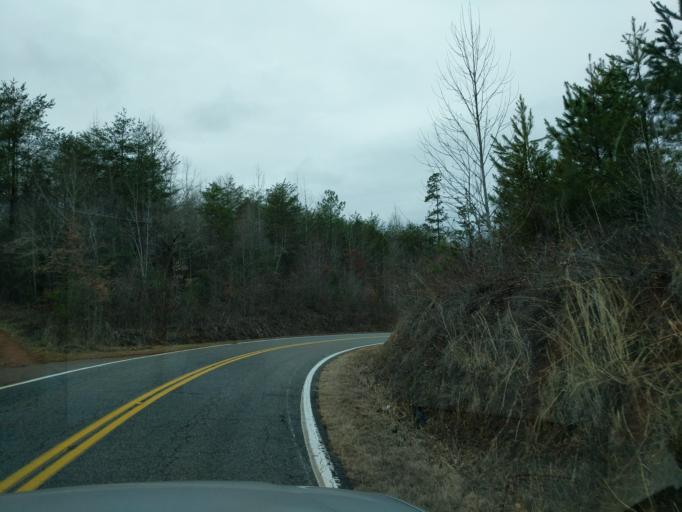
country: US
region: South Carolina
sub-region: Oconee County
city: Walhalla
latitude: 34.7923
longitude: -83.0875
